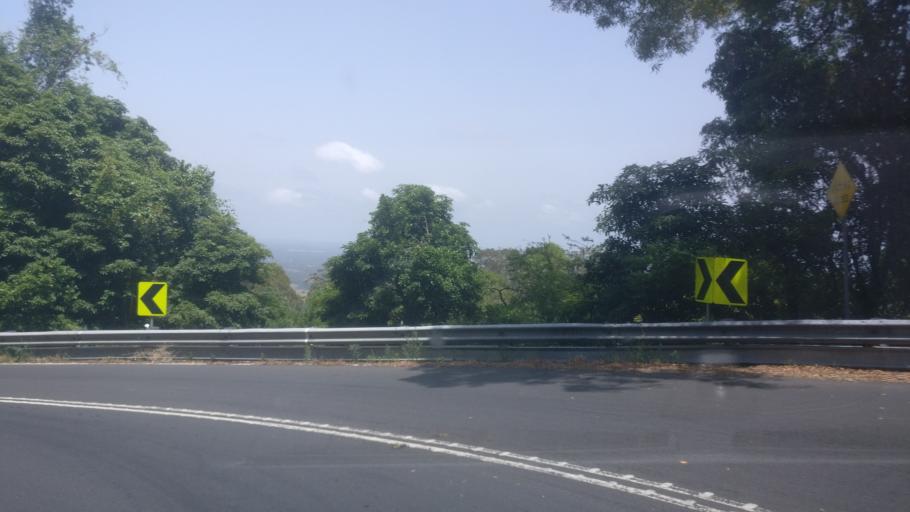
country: AU
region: New South Wales
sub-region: Shoalhaven Shire
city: Kangaroo Valley
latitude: -34.7908
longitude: 150.5585
